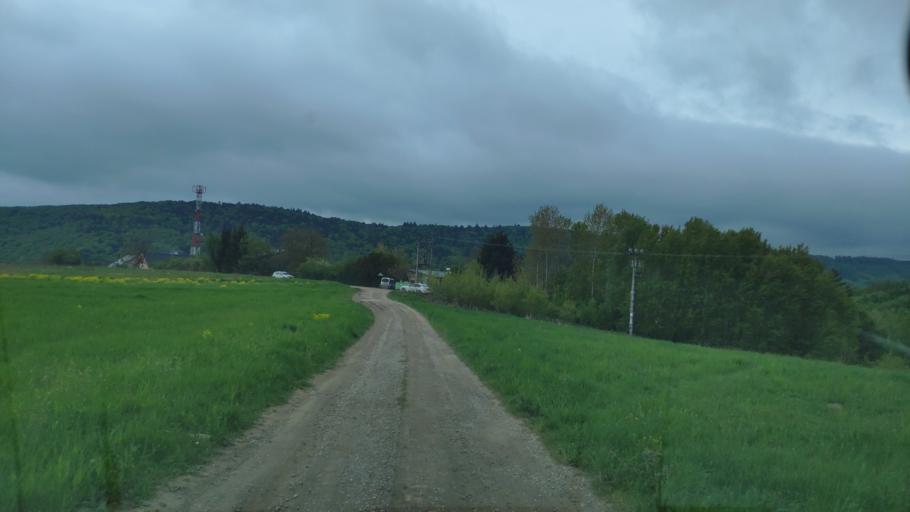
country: SK
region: Kosicky
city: Kosice
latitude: 48.7608
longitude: 21.2012
